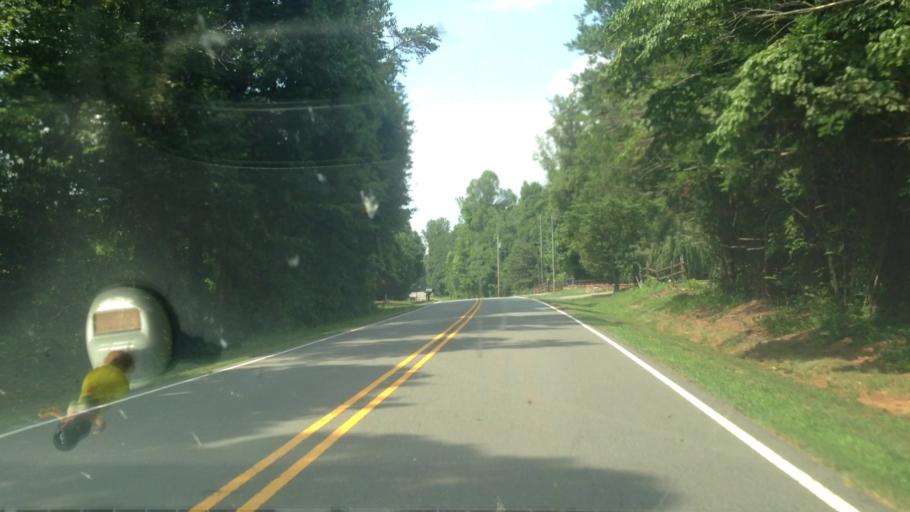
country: US
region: North Carolina
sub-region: Stokes County
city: Walnut Cove
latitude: 36.3952
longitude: -80.0948
